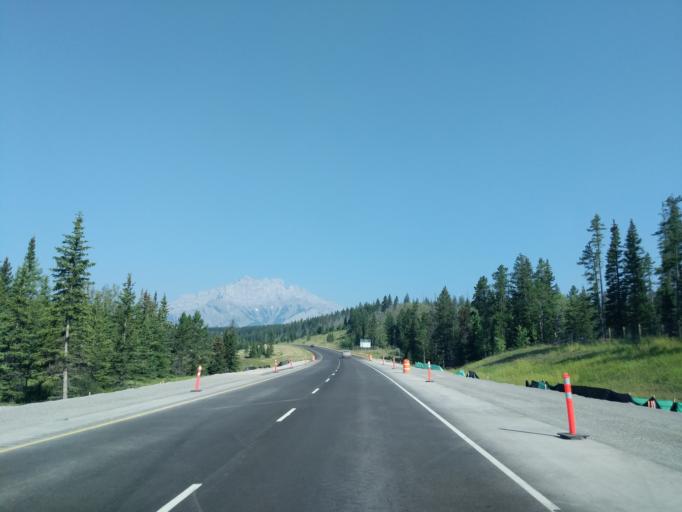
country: CA
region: Alberta
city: Canmore
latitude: 51.1612
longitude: -115.4400
